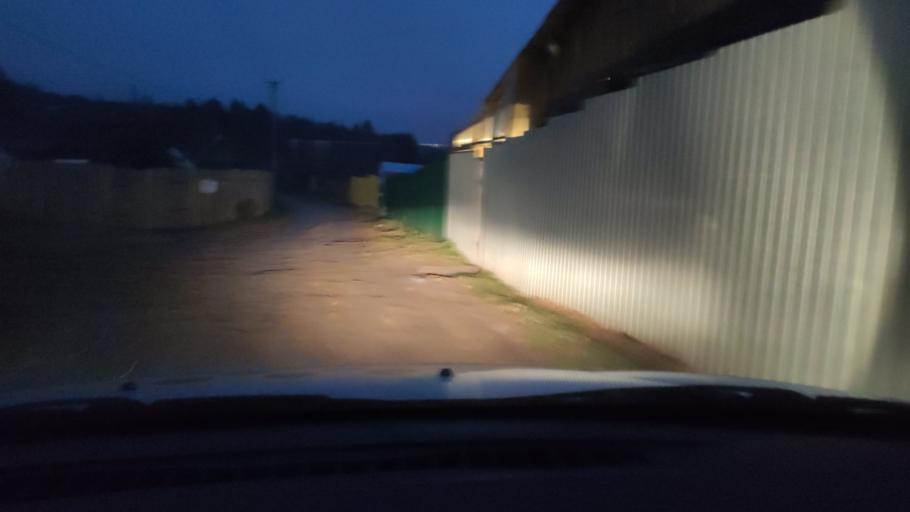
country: RU
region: Perm
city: Kondratovo
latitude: 57.9442
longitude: 56.1837
